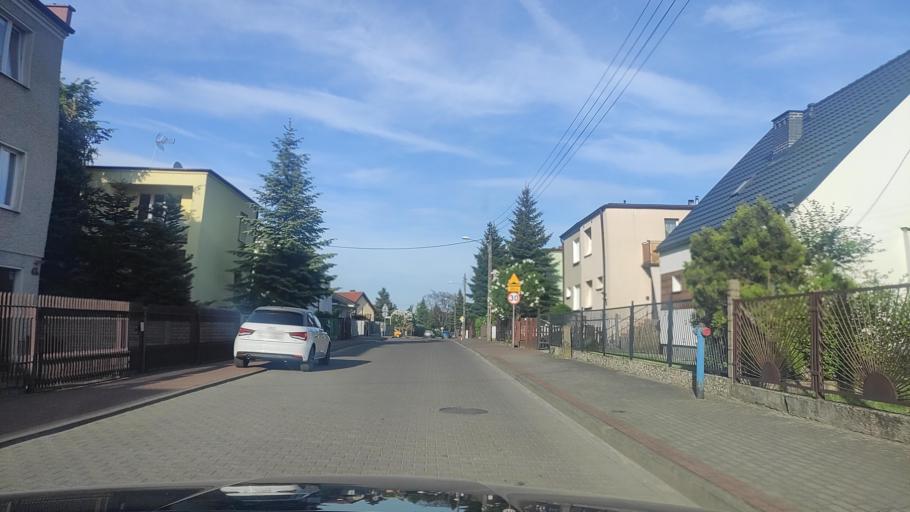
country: PL
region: Greater Poland Voivodeship
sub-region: Powiat poznanski
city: Czerwonak
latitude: 52.4298
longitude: 17.0234
